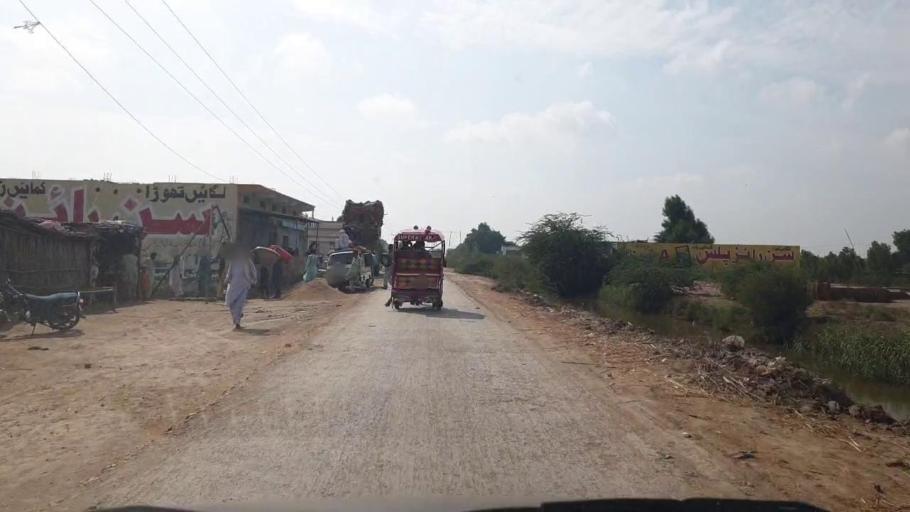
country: PK
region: Sindh
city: Kario
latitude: 24.6529
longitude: 68.5423
